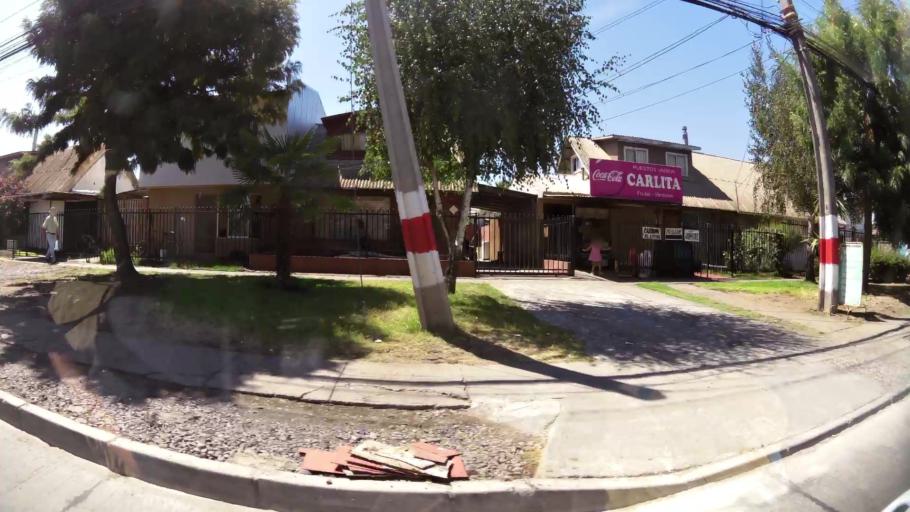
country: CL
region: Maule
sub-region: Provincia de Curico
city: Curico
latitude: -34.9693
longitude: -71.2305
